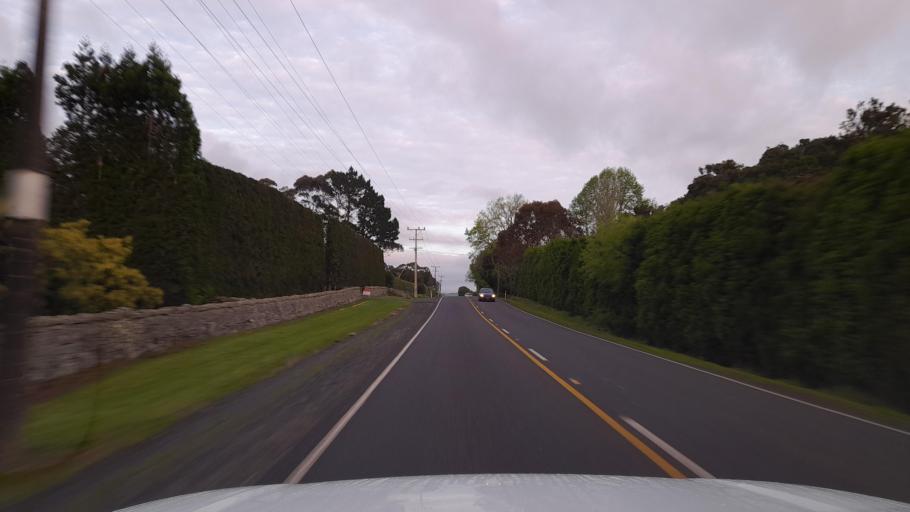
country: NZ
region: Northland
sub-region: Whangarei
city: Maungatapere
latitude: -35.7486
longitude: 174.1615
